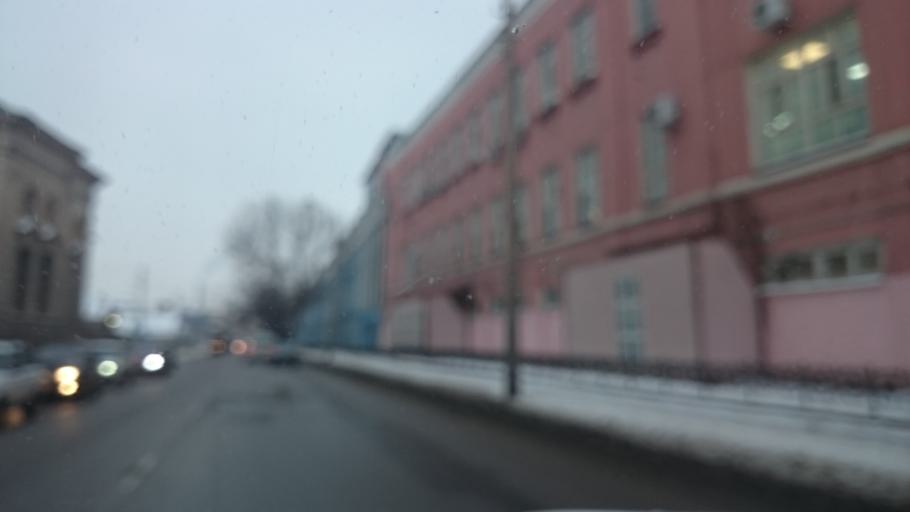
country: RU
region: Tula
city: Tula
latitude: 54.2013
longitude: 37.6114
